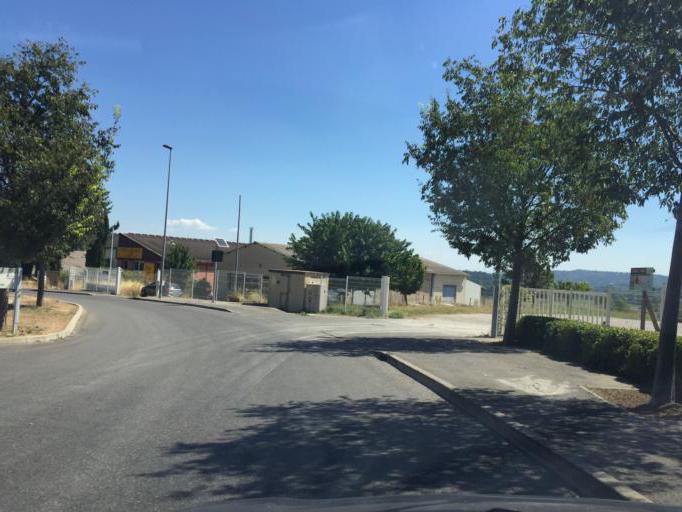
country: FR
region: Provence-Alpes-Cote d'Azur
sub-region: Departement des Alpes-de-Haute-Provence
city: Forcalquier
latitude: 43.9581
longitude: 5.7927
